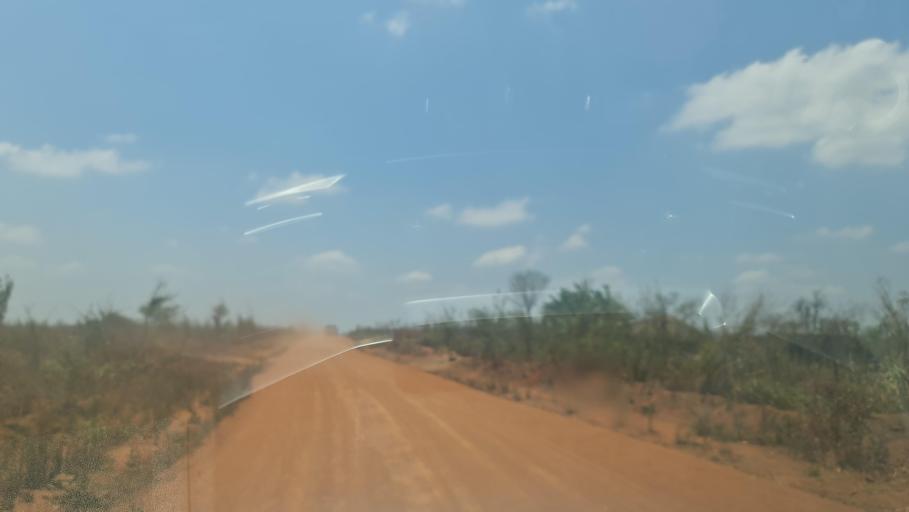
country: MW
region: Southern Region
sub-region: Nsanje District
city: Nsanje
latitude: -17.3487
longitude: 35.7478
